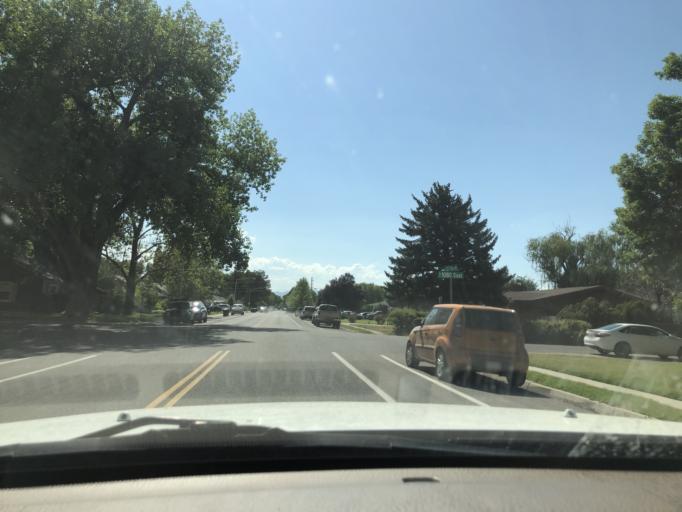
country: US
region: Utah
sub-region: Utah County
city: Provo
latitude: 40.2374
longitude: -111.6397
